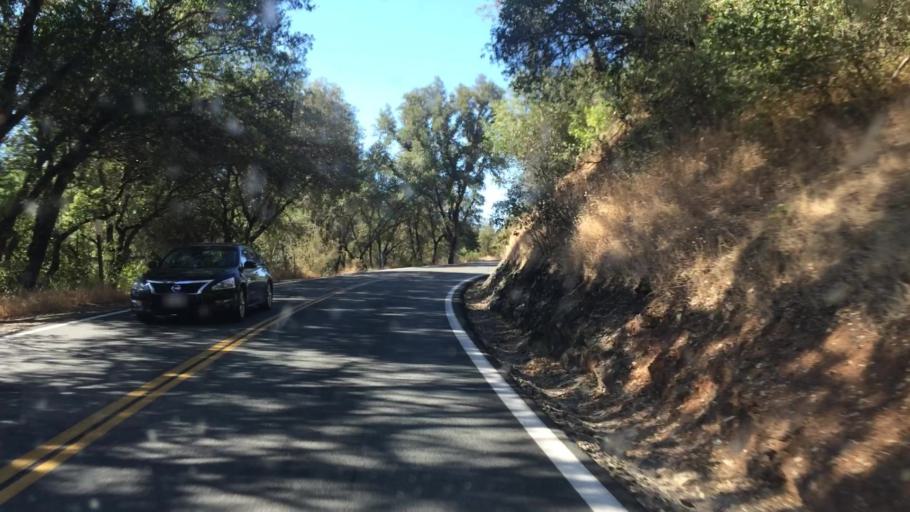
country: US
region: California
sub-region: Amador County
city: Plymouth
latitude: 38.5406
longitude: -120.8475
